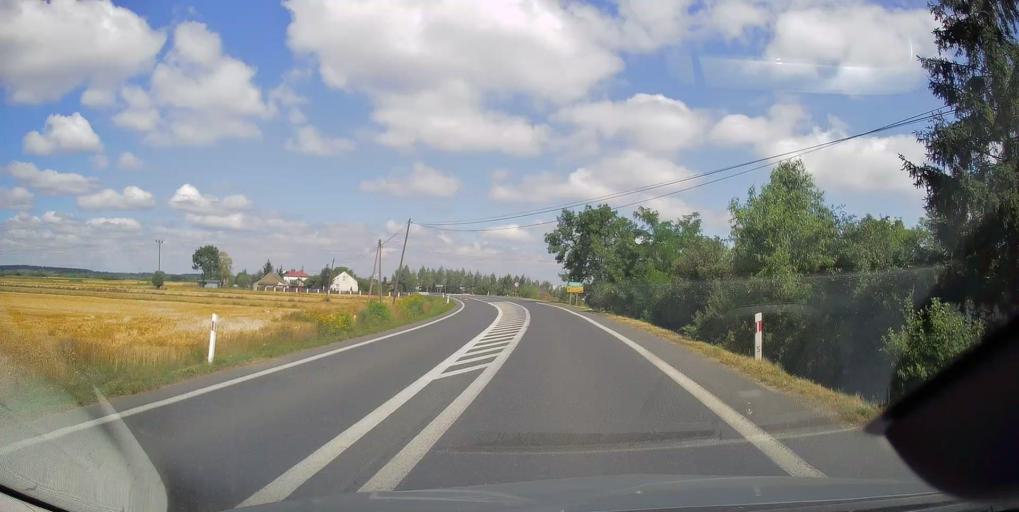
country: PL
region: Subcarpathian Voivodeship
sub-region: Powiat debicki
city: Brzeznica
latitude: 50.1458
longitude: 21.4862
